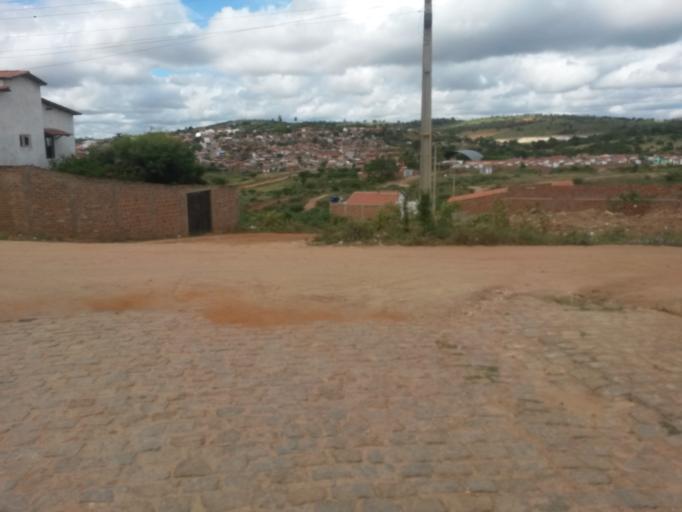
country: BR
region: Bahia
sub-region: Mairi
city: Mairi
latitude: -11.7063
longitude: -40.1525
